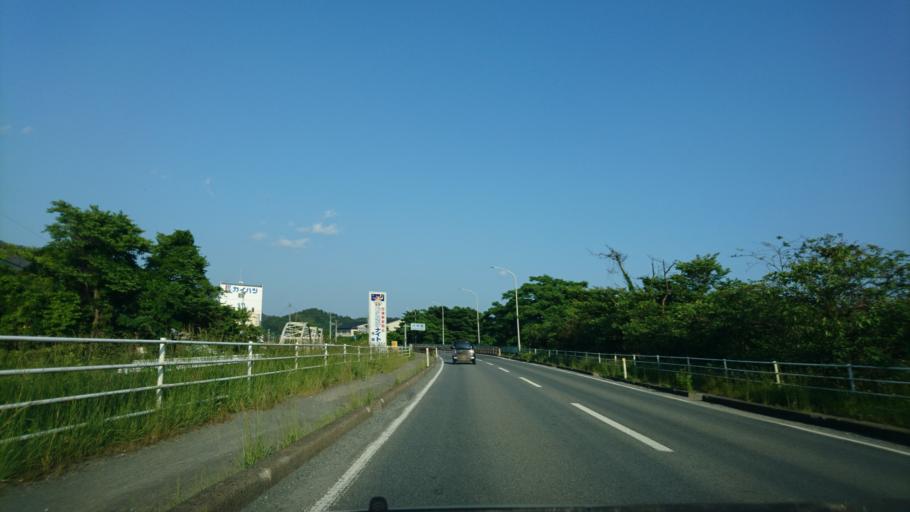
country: JP
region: Iwate
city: Ofunato
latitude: 38.9128
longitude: 141.5381
